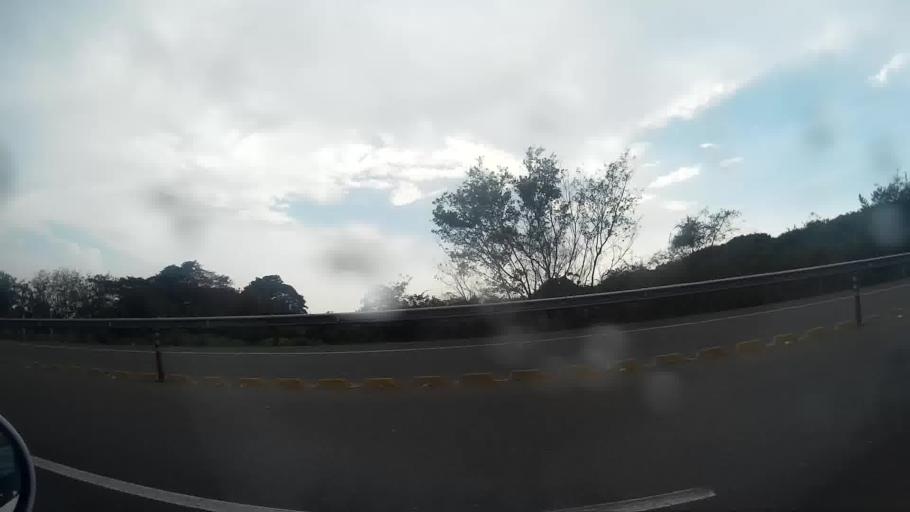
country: CO
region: Magdalena
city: Cienaga
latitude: 11.0102
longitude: -74.2164
